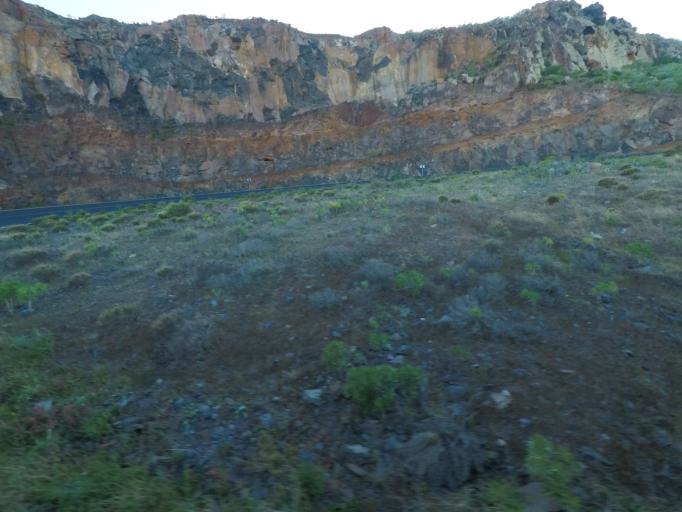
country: ES
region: Canary Islands
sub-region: Provincia de Santa Cruz de Tenerife
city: San Sebastian de la Gomera
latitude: 28.0831
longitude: -17.1324
